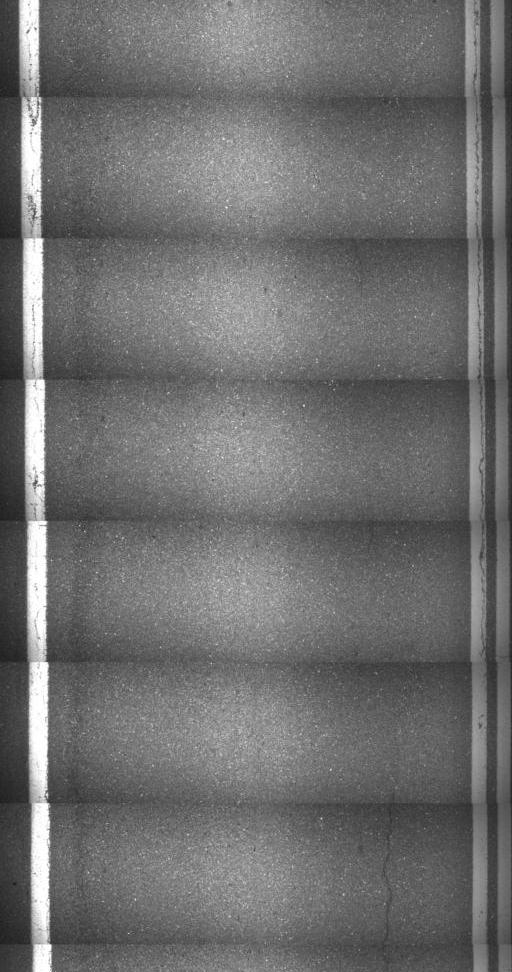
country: US
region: Vermont
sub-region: Windsor County
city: Chester
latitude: 43.2728
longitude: -72.5696
